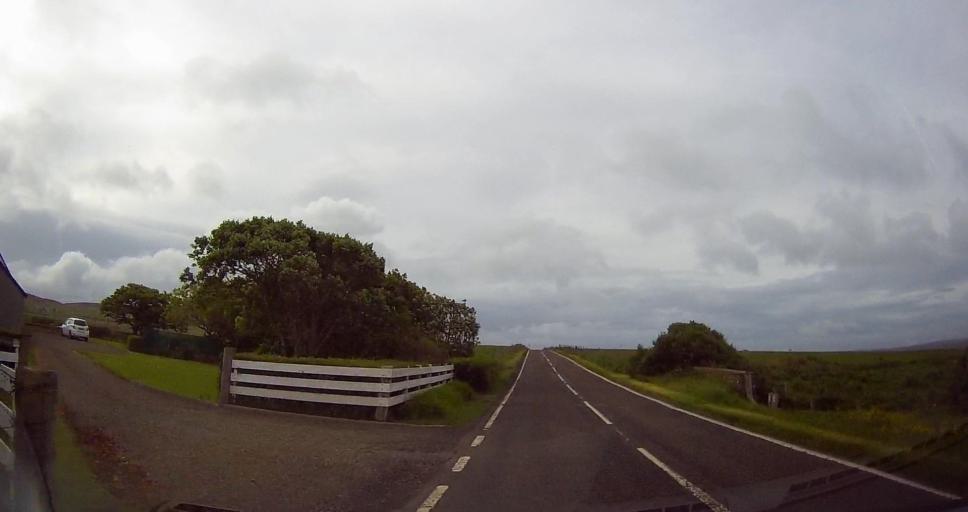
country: GB
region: Scotland
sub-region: Orkney Islands
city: Stromness
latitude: 58.9377
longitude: -3.2133
